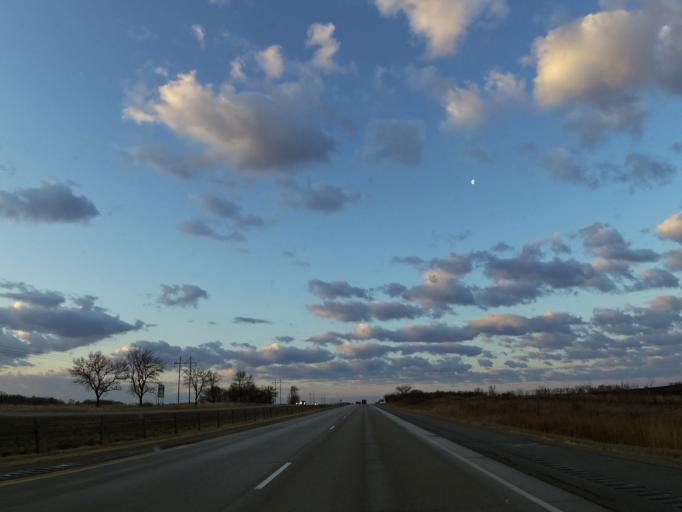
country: US
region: Minnesota
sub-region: Rice County
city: Dundas
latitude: 44.4396
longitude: -93.2927
